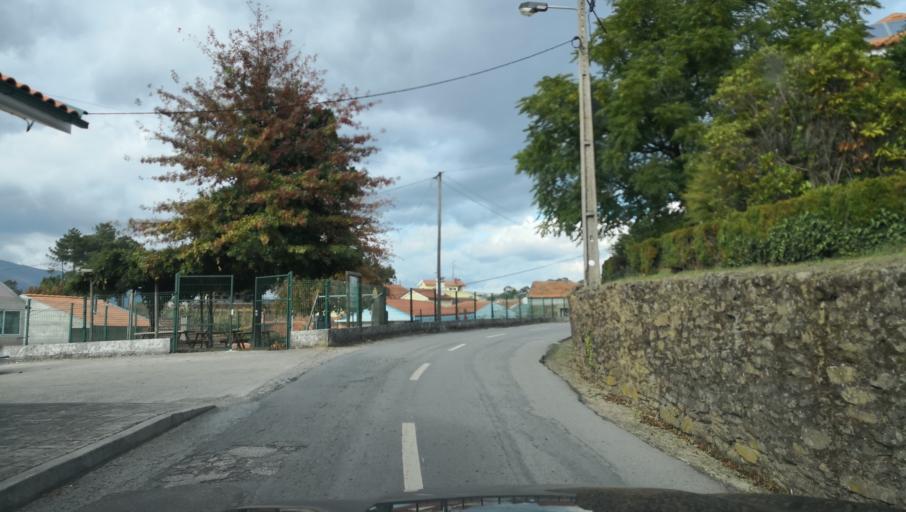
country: PT
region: Vila Real
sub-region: Vila Real
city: Vila Real
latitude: 41.2881
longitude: -7.7174
